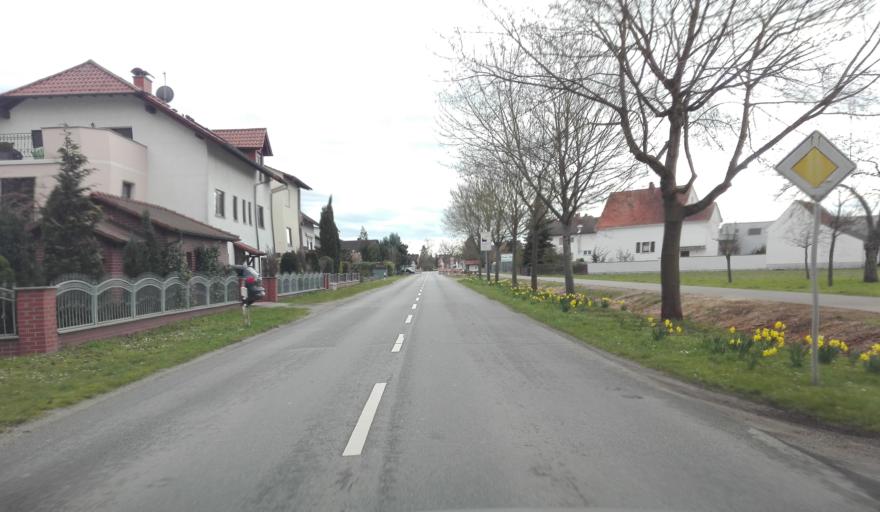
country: DE
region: Hesse
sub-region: Regierungsbezirk Darmstadt
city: Alsbach-Hahnlein
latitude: 49.7106
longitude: 8.5746
